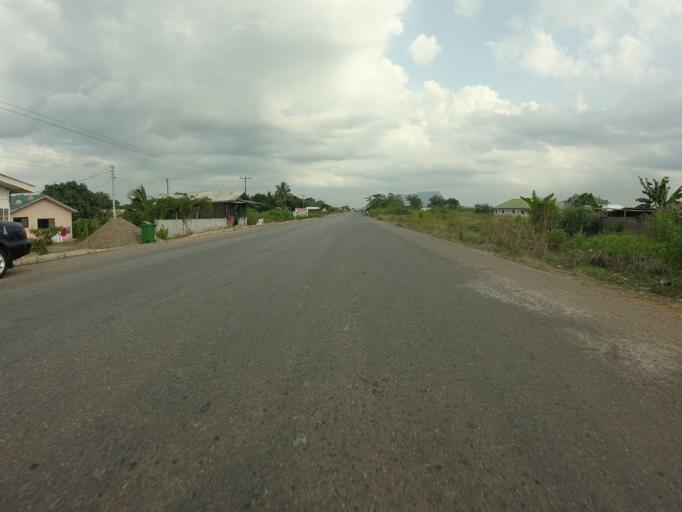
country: GH
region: Volta
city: Ho
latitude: 6.5777
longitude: 0.4828
